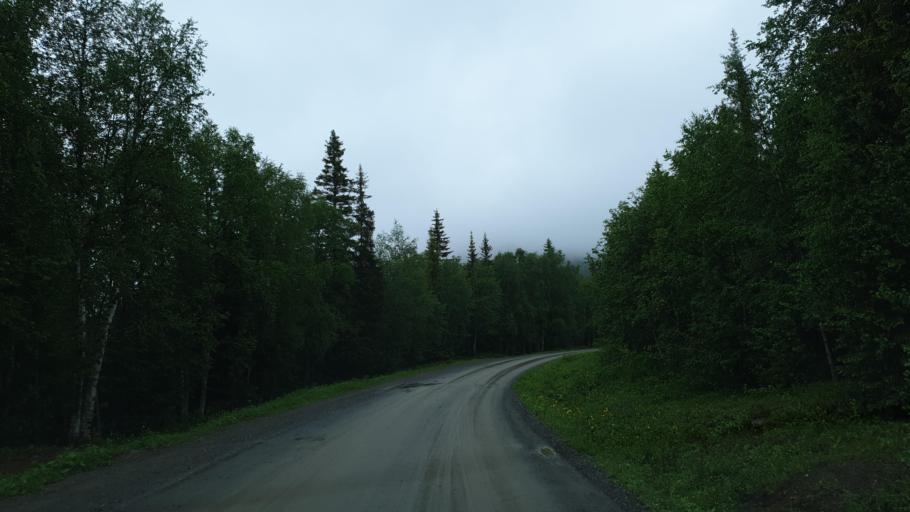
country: SE
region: Vaesterbotten
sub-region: Vilhelmina Kommun
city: Sjoberg
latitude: 65.3401
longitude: 15.8717
